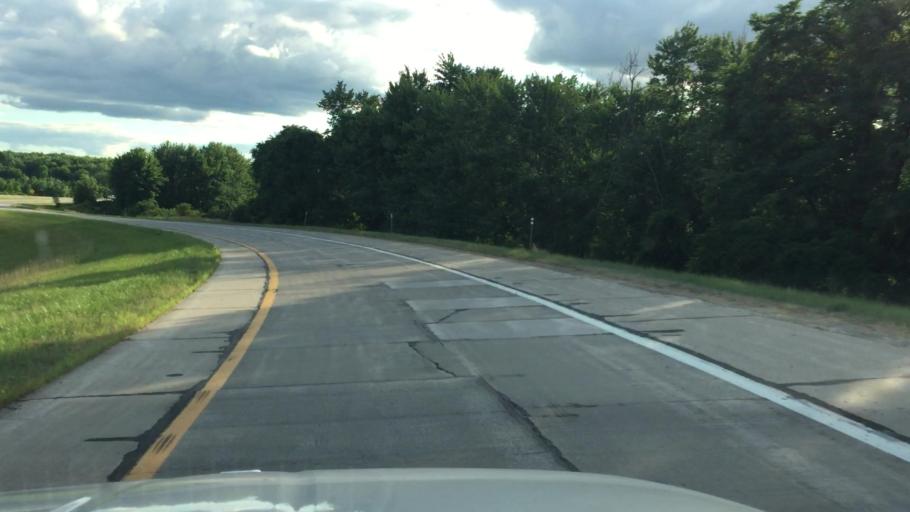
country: US
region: Michigan
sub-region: Macomb County
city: Memphis
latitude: 42.9821
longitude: -82.7668
